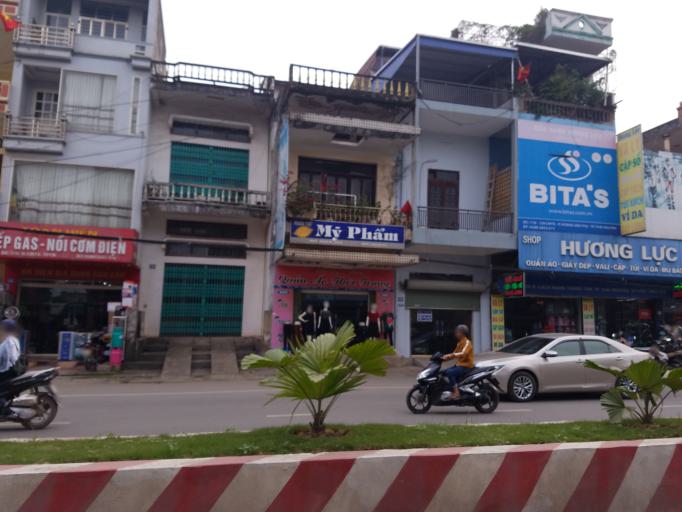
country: VN
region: Thai Nguyen
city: Thanh Pho Thai Nguyen
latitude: 21.5918
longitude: 105.8439
